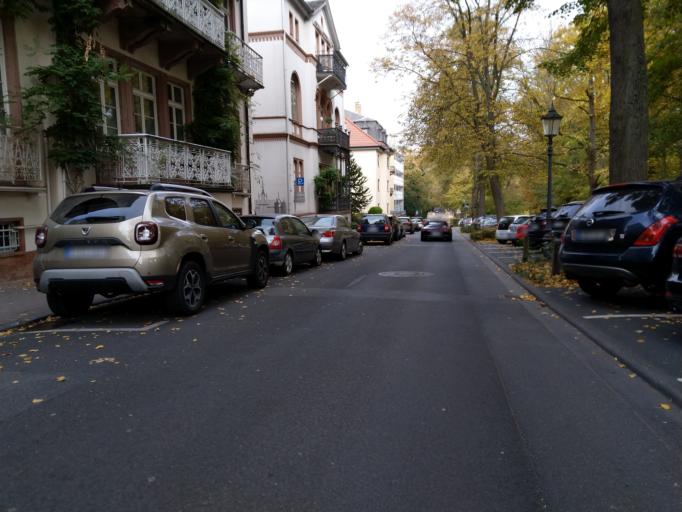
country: DE
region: Hesse
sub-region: Regierungsbezirk Darmstadt
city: Bad Homburg vor der Hoehe
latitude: 50.2289
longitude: 8.6184
